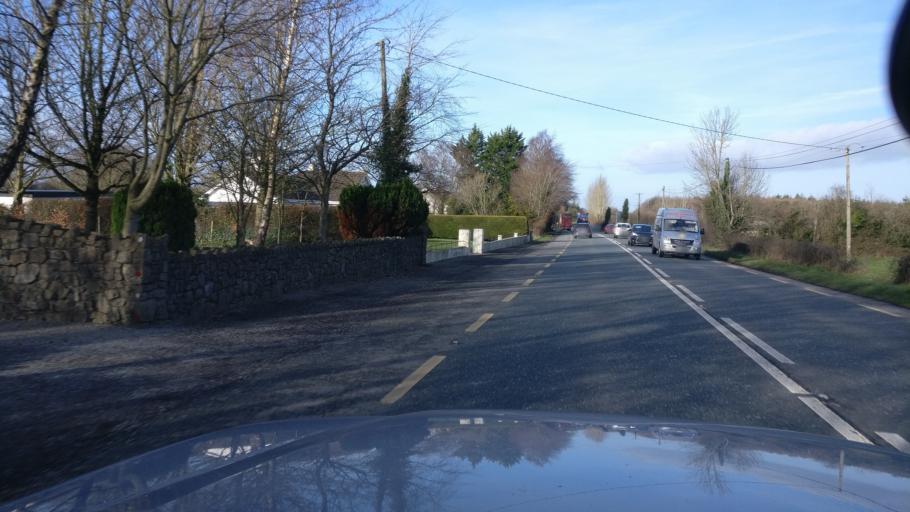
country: IE
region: Leinster
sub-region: Uibh Fhaili
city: Tullamore
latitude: 53.2239
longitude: -7.4758
